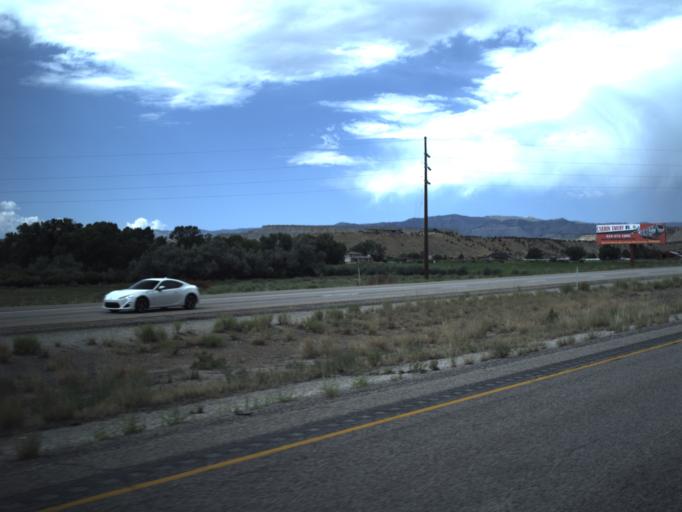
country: US
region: Utah
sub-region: Carbon County
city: Carbonville
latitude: 39.6162
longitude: -110.8459
